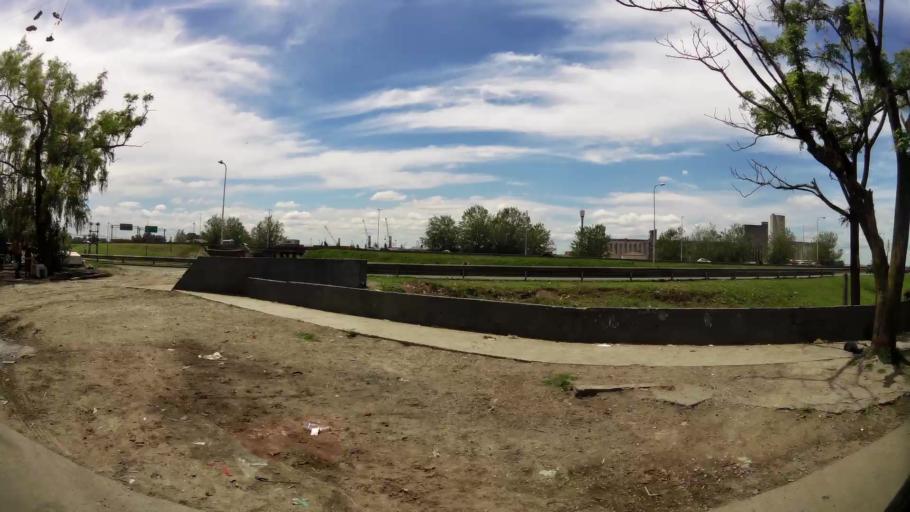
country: AR
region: Santa Fe
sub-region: Departamento de Rosario
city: Rosario
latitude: -32.9814
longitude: -60.6261
